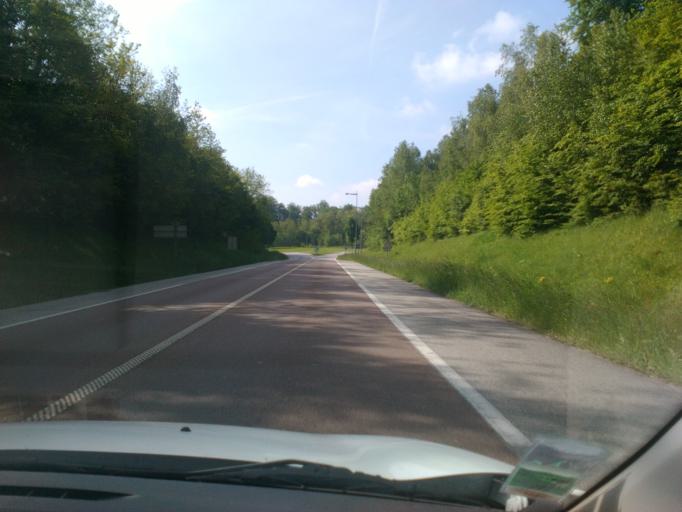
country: FR
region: Lorraine
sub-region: Departement des Vosges
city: Les Forges
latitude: 48.1929
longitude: 6.4000
